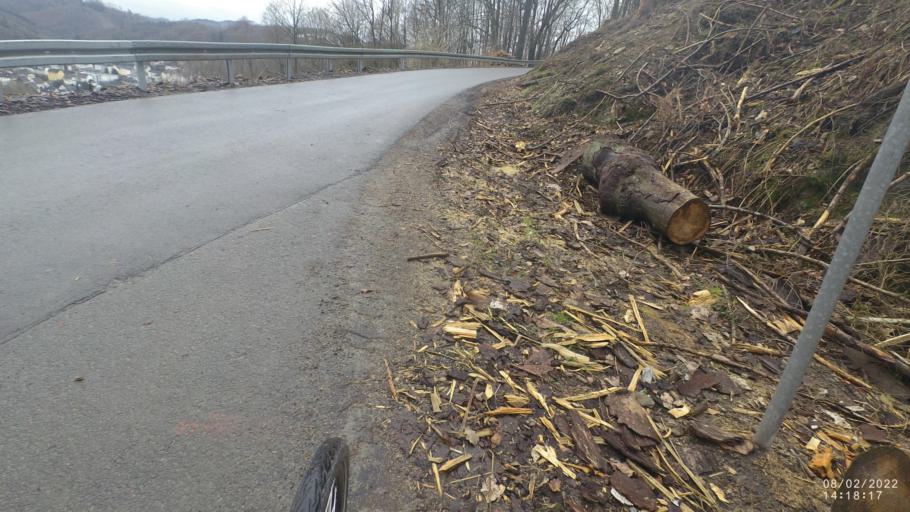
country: DE
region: North Rhine-Westphalia
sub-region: Regierungsbezirk Arnsberg
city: Schalksmuhle
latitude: 51.2483
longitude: 7.5250
